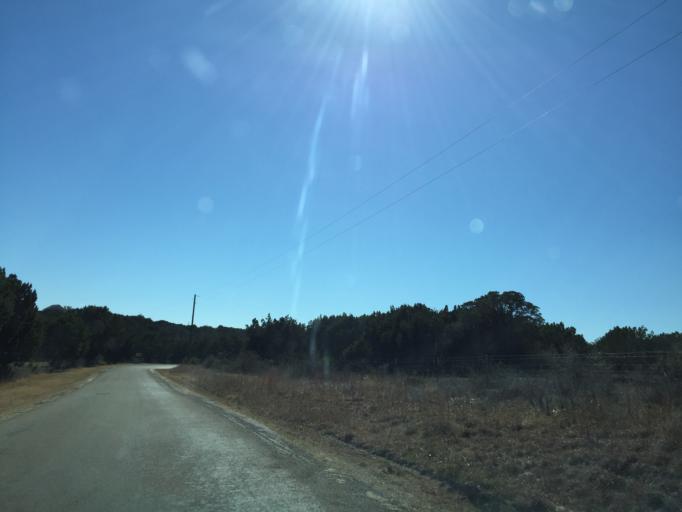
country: US
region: Texas
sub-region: Burnet County
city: Bertram
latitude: 30.9002
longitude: -98.1188
